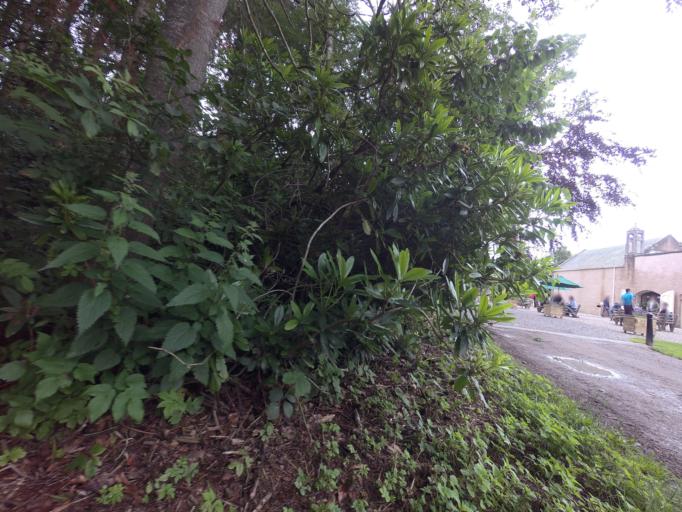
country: GB
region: Scotland
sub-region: Moray
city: Forres
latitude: 57.5987
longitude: -3.7096
